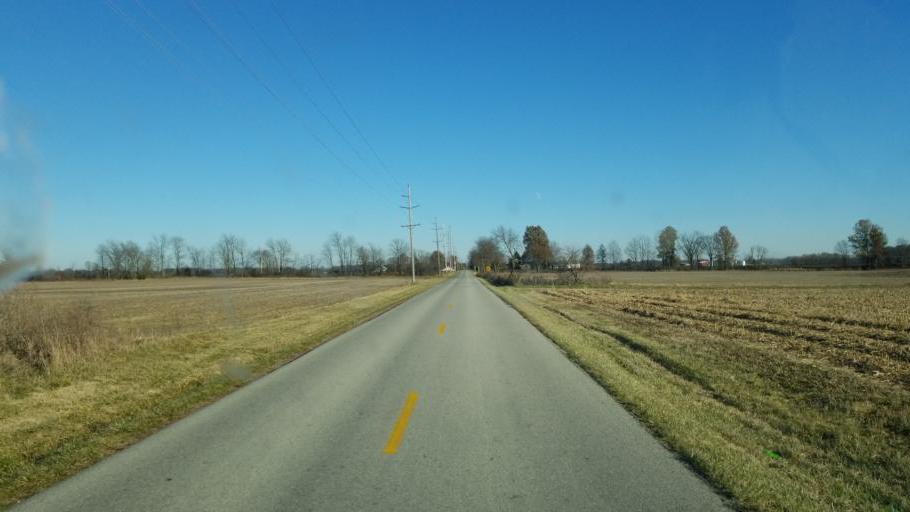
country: US
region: Ohio
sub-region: Morrow County
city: Cardington
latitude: 40.4683
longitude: -82.9215
